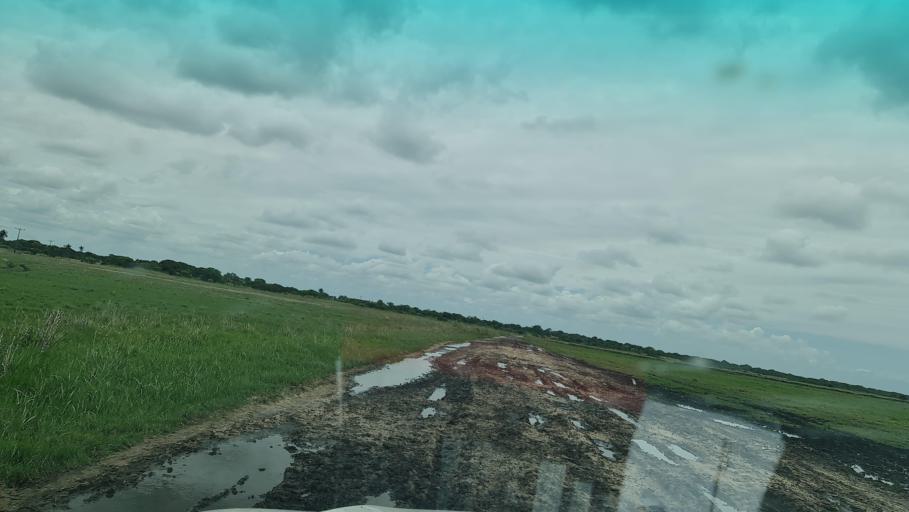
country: MZ
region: Maputo City
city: Maputo
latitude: -25.7068
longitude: 32.7033
